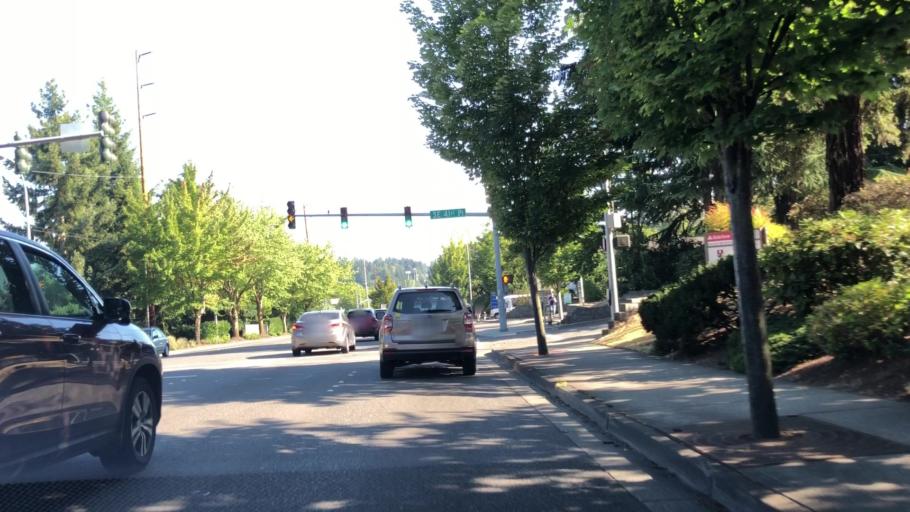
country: US
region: Washington
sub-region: King County
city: Newport
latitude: 47.5716
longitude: -122.1694
